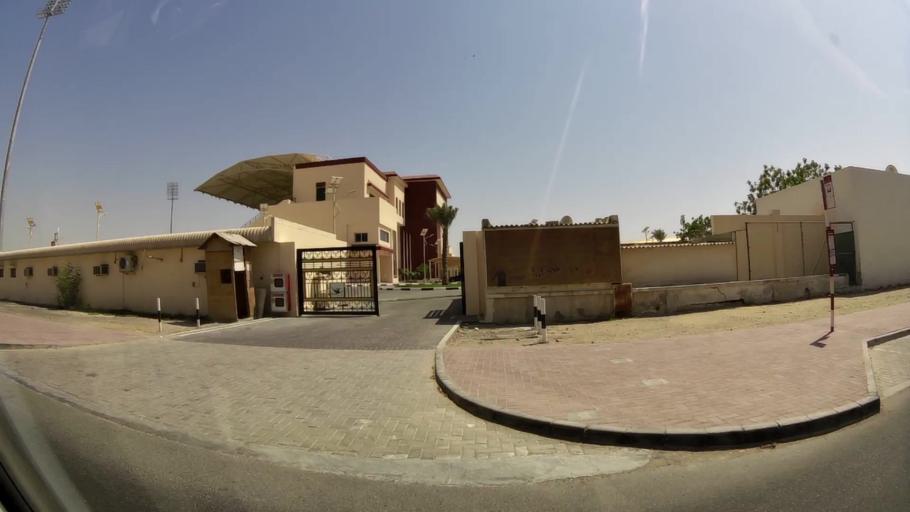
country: AE
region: Ash Shariqah
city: Sharjah
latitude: 25.2796
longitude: 55.3646
